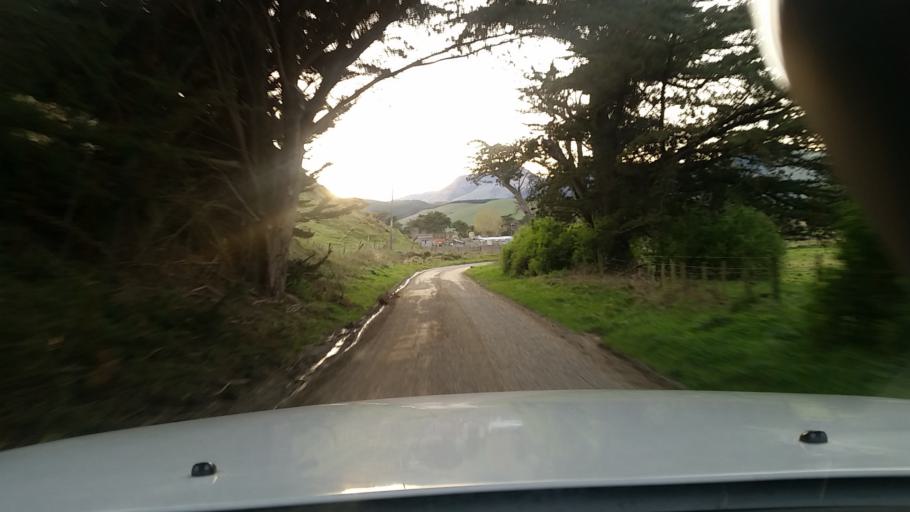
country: NZ
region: Canterbury
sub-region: Selwyn District
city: Lincoln
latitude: -43.7203
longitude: 172.5924
